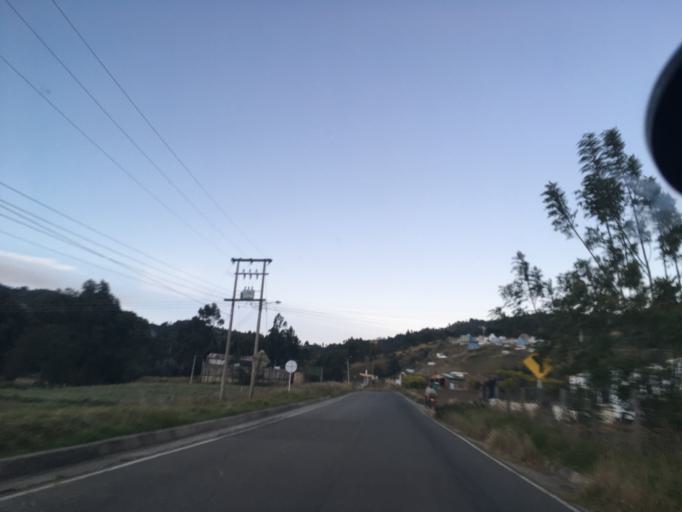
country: CO
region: Boyaca
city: Aquitania
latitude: 5.6005
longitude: -72.9106
